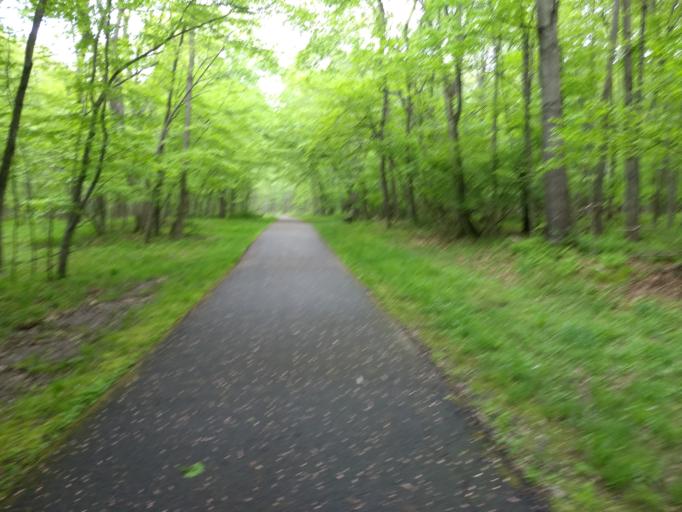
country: US
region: New Jersey
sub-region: Morris County
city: Morris Plains
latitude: 40.8142
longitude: -74.5070
